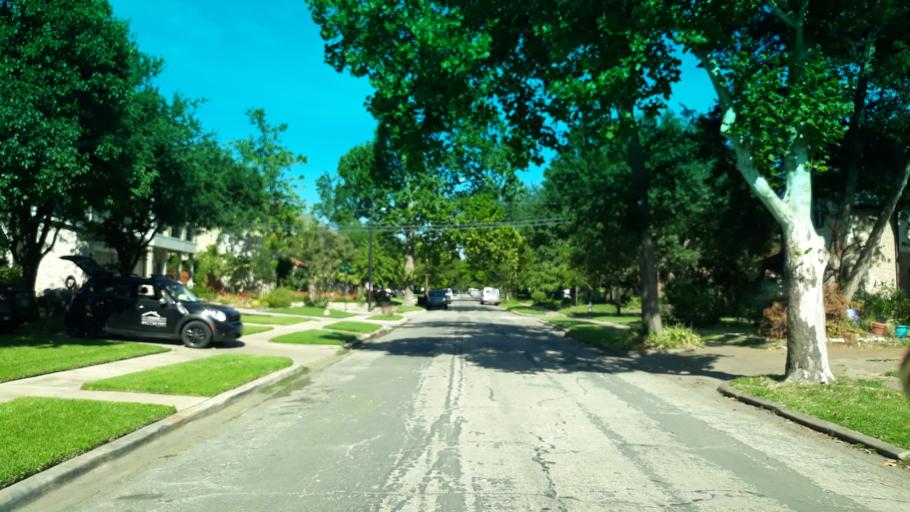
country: US
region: Texas
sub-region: Dallas County
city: Highland Park
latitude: 32.8201
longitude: -96.7593
